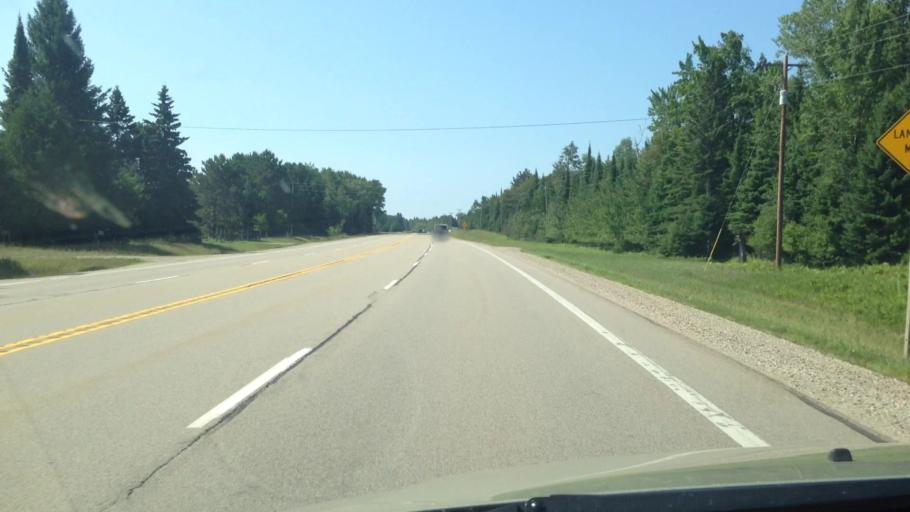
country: US
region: Michigan
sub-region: Delta County
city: Escanaba
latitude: 45.5309
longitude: -87.2862
